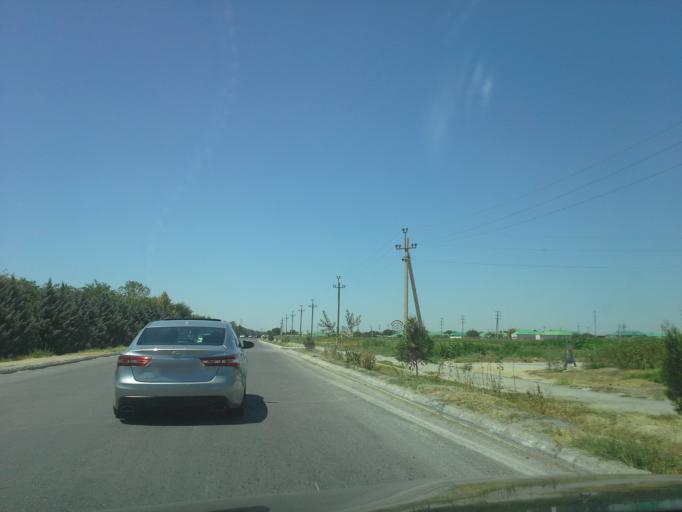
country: TM
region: Ahal
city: Abadan
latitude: 38.0293
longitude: 58.2344
